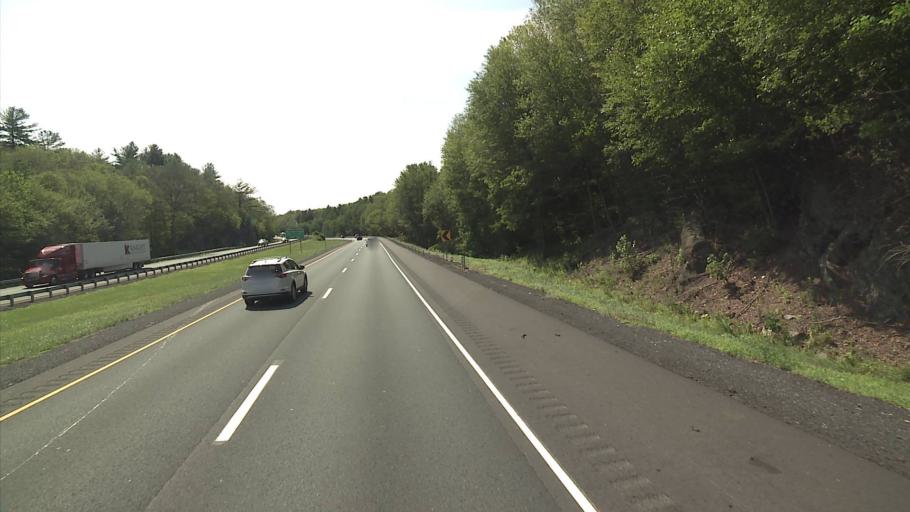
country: US
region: Connecticut
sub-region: Hartford County
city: Terramuggus
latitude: 41.6547
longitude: -72.5024
